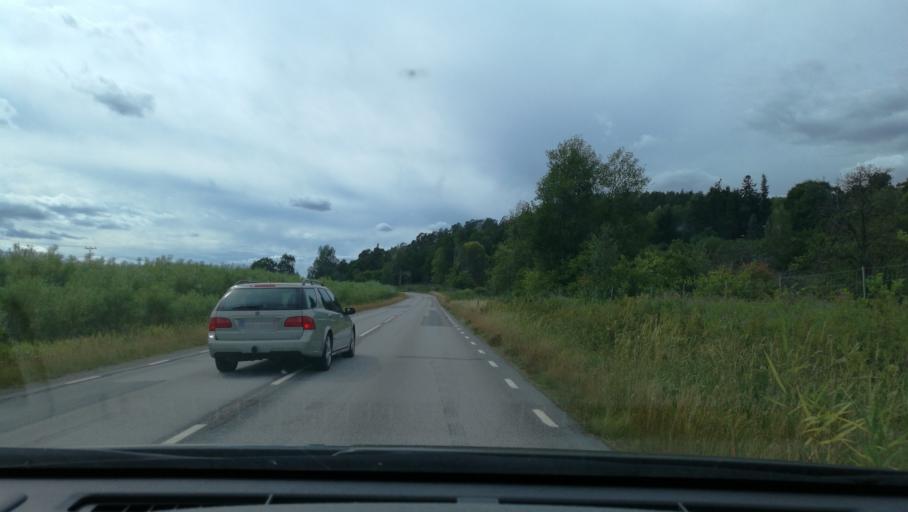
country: SE
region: OEstergoetland
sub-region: Norrkopings Kommun
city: Jursla
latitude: 58.6674
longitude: 16.2150
